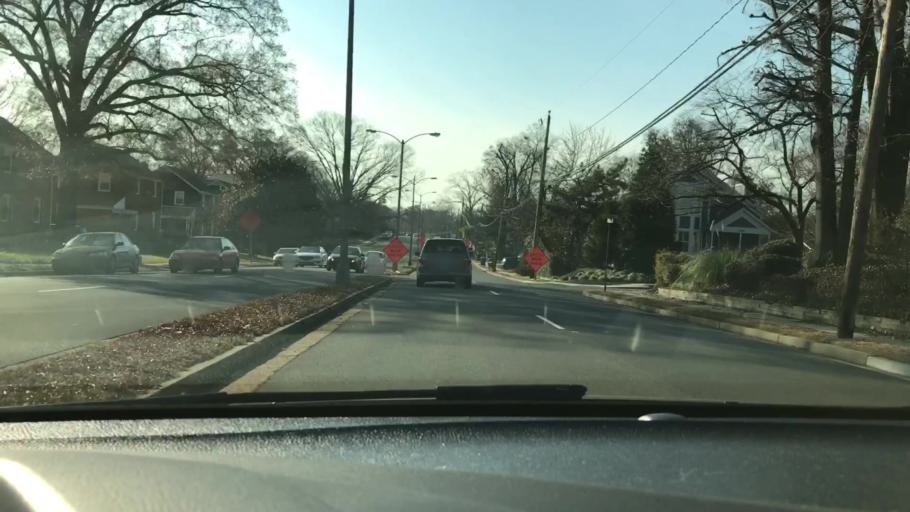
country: US
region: Virginia
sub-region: Arlington County
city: Arlington
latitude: 38.8728
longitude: -77.1204
